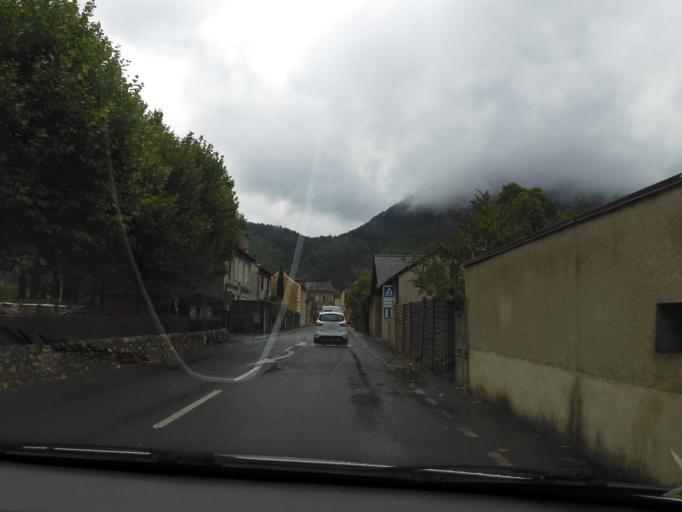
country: FR
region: Languedoc-Roussillon
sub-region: Departement de la Lozere
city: Florac
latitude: 44.3718
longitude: 3.5336
